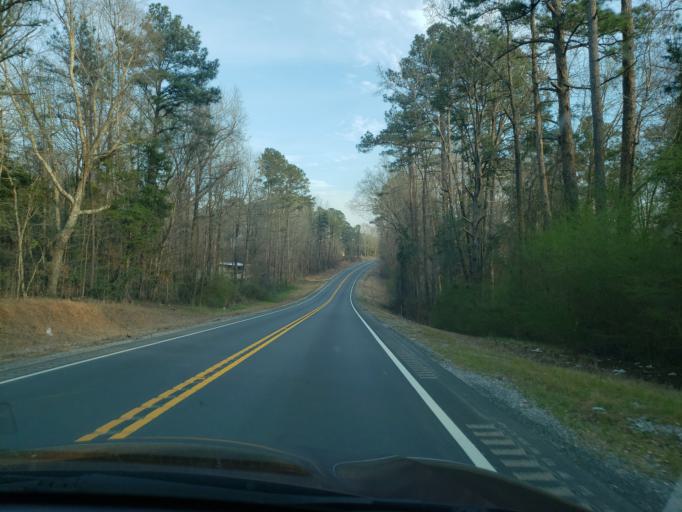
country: US
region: Alabama
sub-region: Hale County
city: Moundville
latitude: 32.8911
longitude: -87.6135
